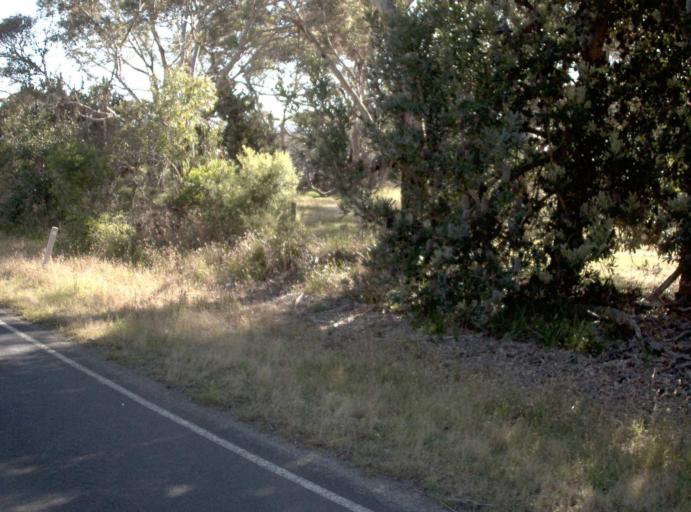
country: AU
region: Victoria
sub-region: Latrobe
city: Morwell
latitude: -38.6953
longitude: 146.3999
